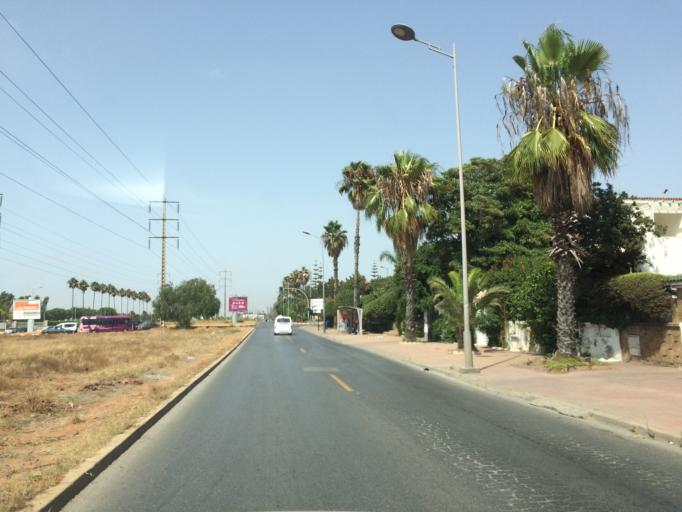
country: MA
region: Rabat-Sale-Zemmour-Zaer
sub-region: Skhirate-Temara
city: Temara
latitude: 33.9635
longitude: -6.8719
